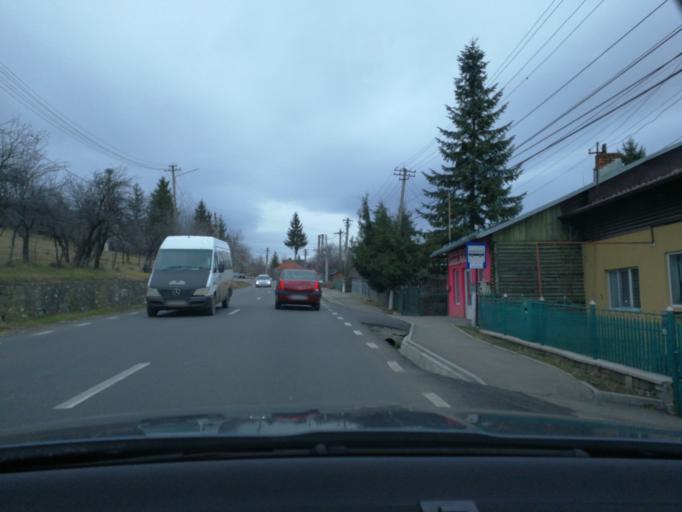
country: RO
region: Prahova
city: Cornu de Sus
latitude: 45.1592
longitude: 25.6863
